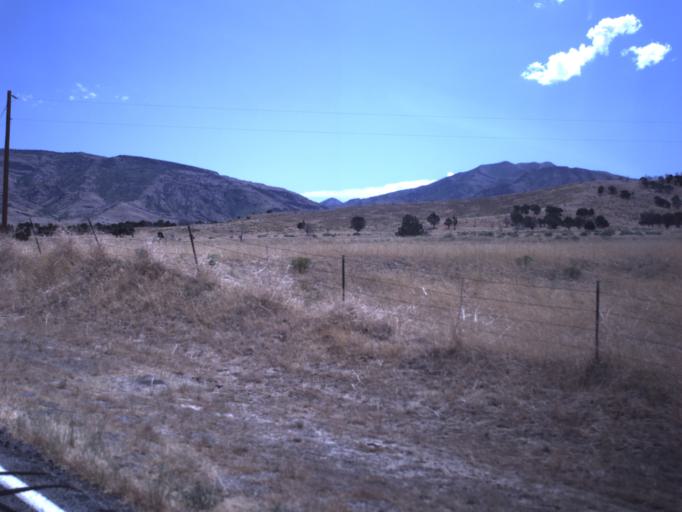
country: US
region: Utah
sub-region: Millard County
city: Delta
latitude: 39.3621
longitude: -112.3500
